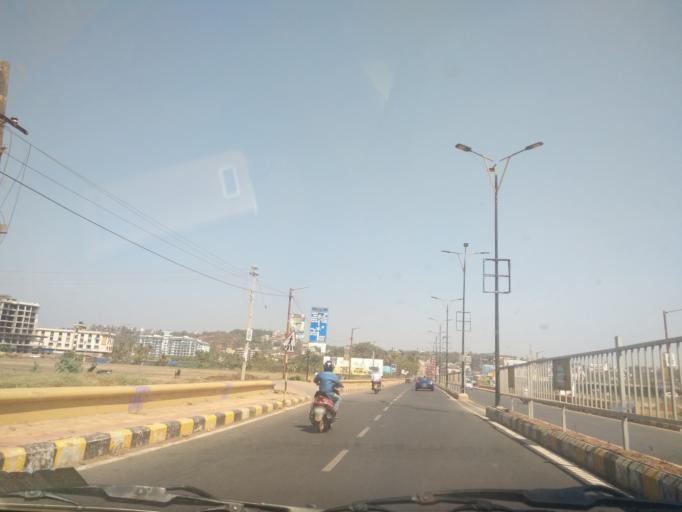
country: IN
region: Goa
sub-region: North Goa
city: Mapuca
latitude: 15.5841
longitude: 73.8073
